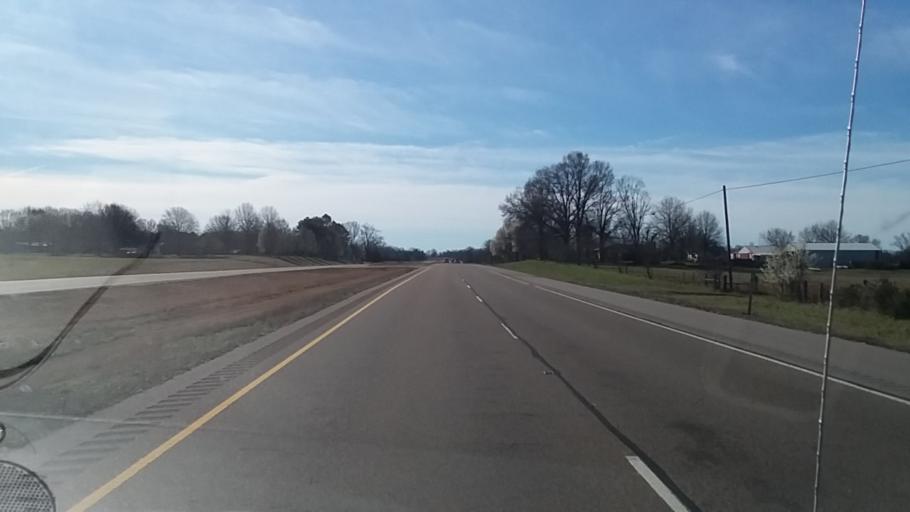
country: US
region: Tennessee
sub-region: Crockett County
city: Alamo
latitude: 35.8498
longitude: -89.1954
